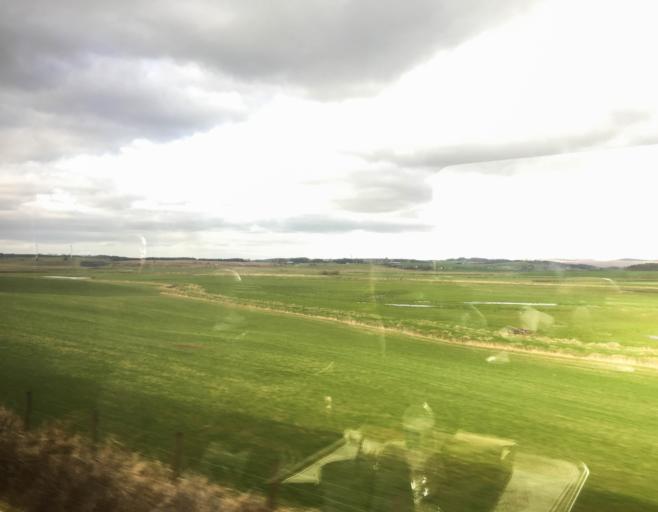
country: GB
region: Scotland
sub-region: South Lanarkshire
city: Carnwath
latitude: 55.6692
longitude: -3.6384
